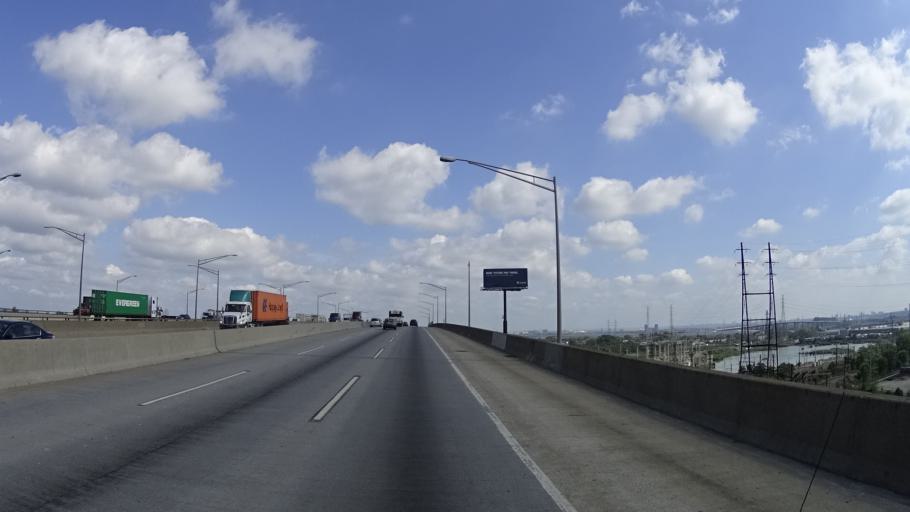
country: US
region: New Jersey
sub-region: Hudson County
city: Harrison
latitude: 40.7415
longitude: -74.1226
